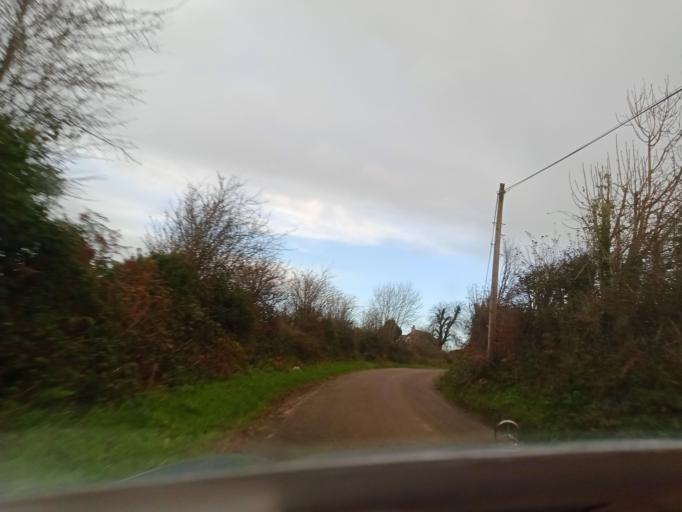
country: IE
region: Munster
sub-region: Waterford
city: Waterford
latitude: 52.3141
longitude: -7.0470
